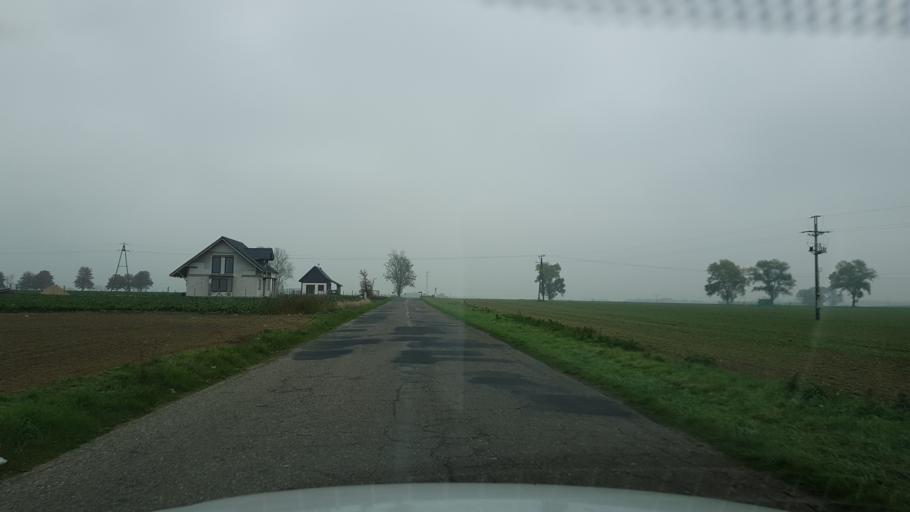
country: PL
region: West Pomeranian Voivodeship
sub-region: Powiat stargardzki
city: Stargard Szczecinski
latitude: 53.2586
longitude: 15.0938
